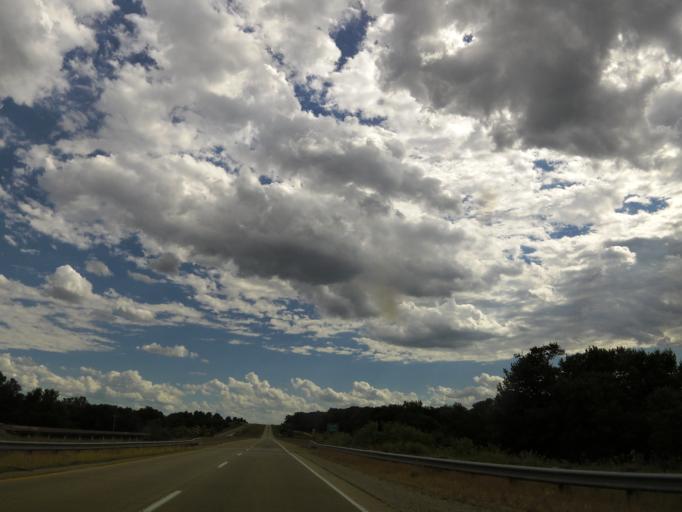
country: US
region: Iowa
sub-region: Henry County
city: Mount Pleasant
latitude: 40.8991
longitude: -91.5543
